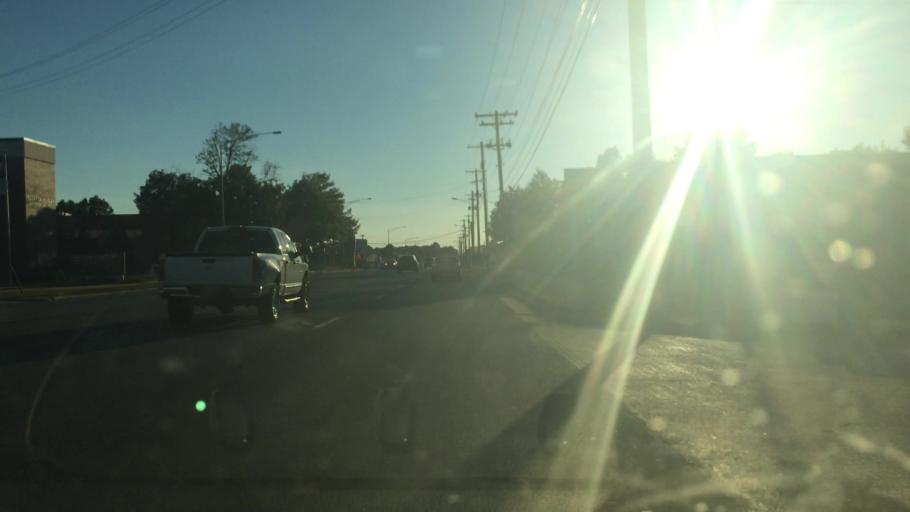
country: US
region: Missouri
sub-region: Greene County
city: Springfield
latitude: 37.1818
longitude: -93.2657
